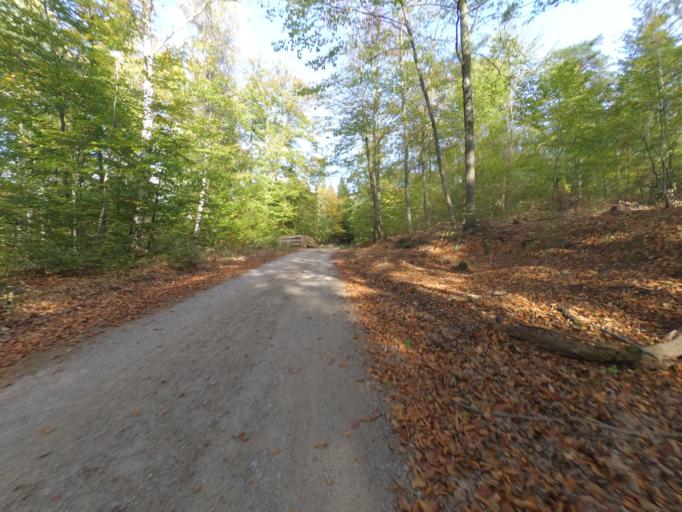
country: DE
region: Saxony
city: Albertstadt
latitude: 51.0986
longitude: 13.8051
